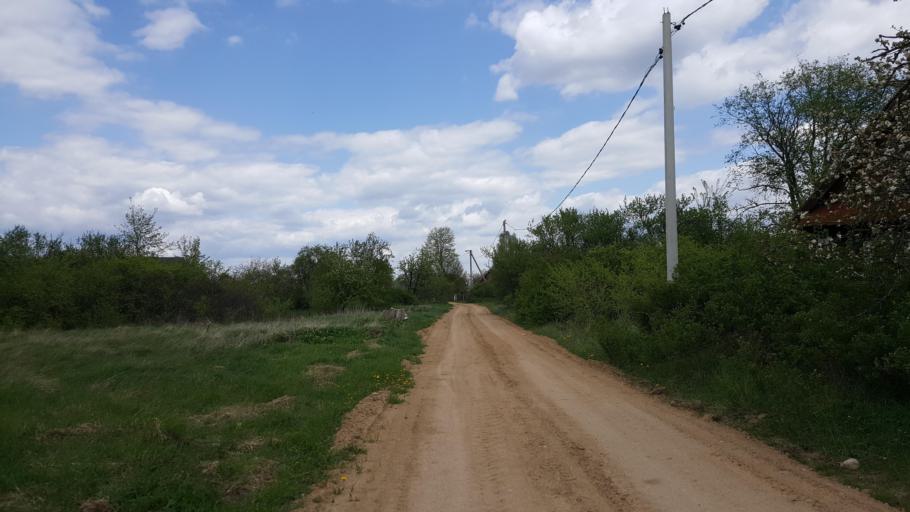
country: BY
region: Brest
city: Zhabinka
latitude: 52.3909
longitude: 24.0983
